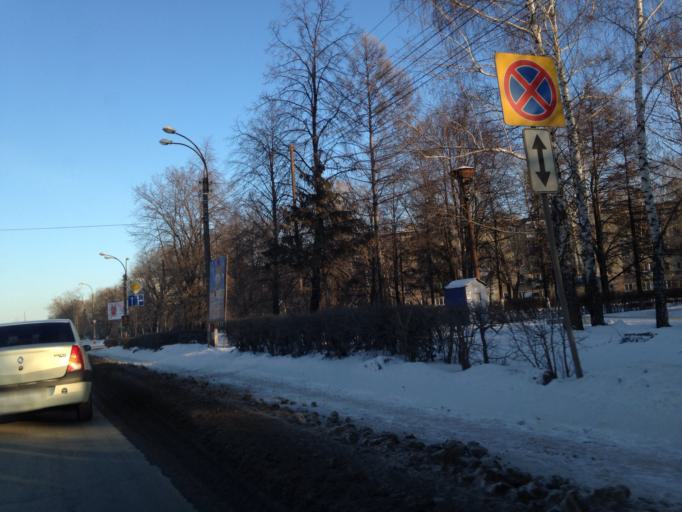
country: RU
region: Ulyanovsk
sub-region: Ulyanovskiy Rayon
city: Ulyanovsk
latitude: 54.2881
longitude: 48.3641
